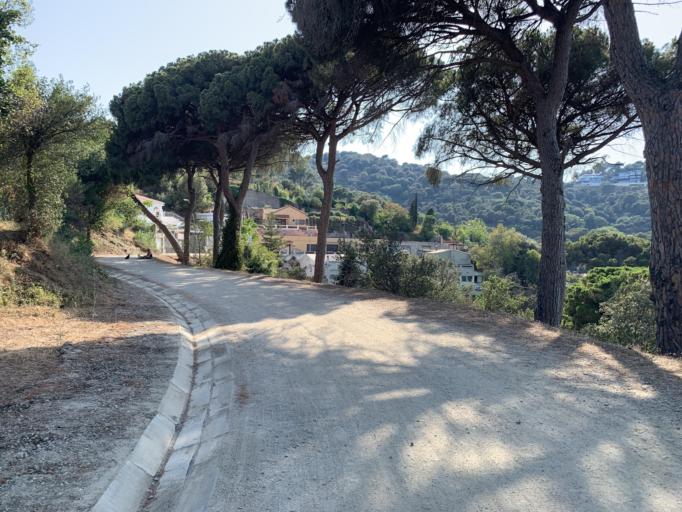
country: ES
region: Catalonia
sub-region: Provincia de Barcelona
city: les Corts
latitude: 41.4071
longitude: 2.1086
